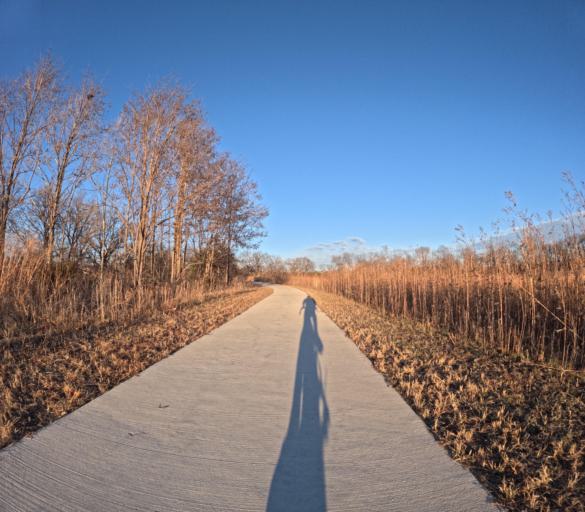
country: US
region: Kansas
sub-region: Riley County
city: Manhattan
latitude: 39.1843
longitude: -96.6361
